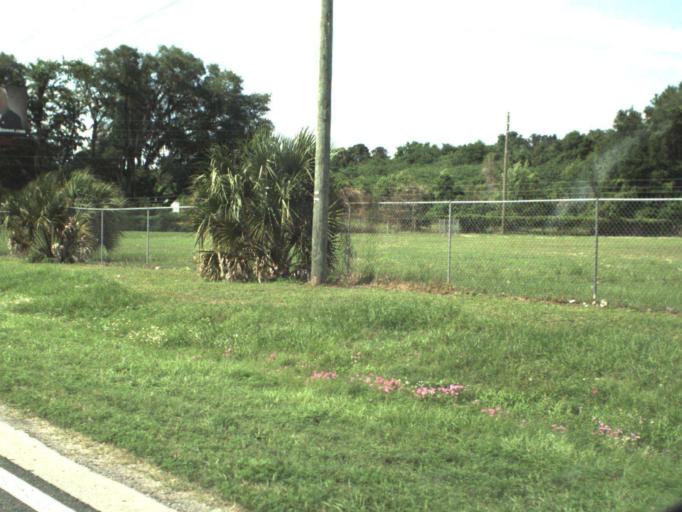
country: US
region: Florida
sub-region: Marion County
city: Ocala
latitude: 29.1377
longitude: -82.1091
